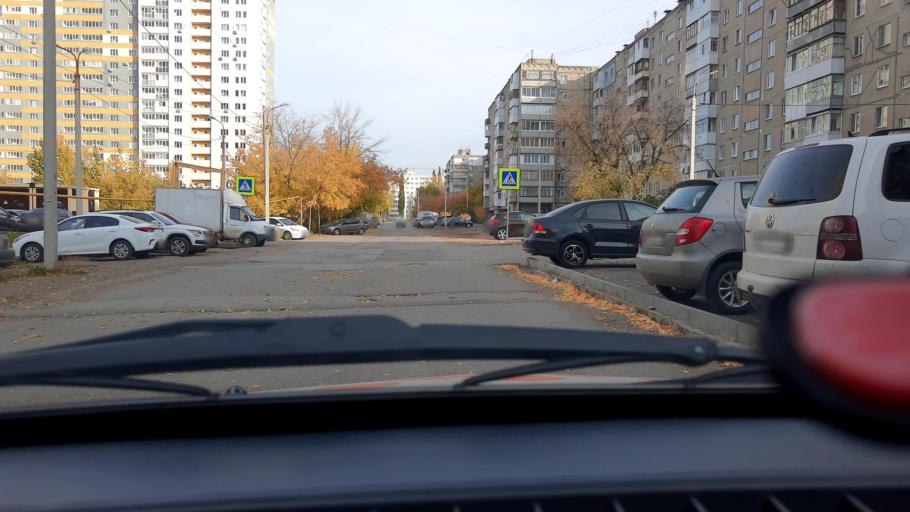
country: RU
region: Bashkortostan
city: Ufa
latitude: 54.7834
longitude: 56.1183
